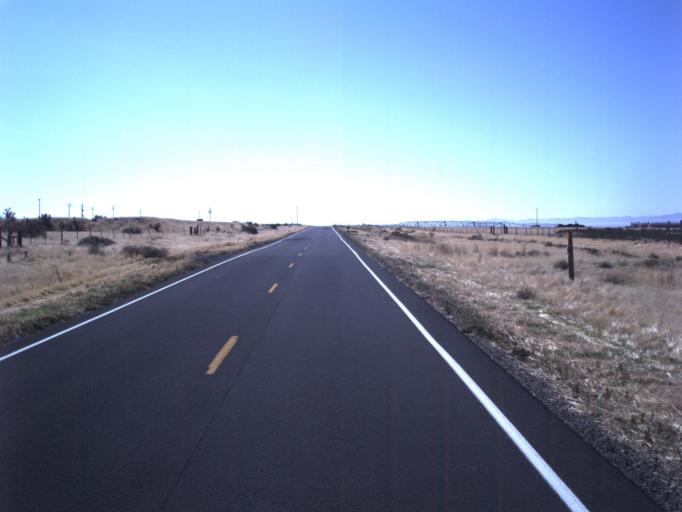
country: US
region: Utah
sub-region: Tooele County
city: Grantsville
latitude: 40.5276
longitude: -112.7477
